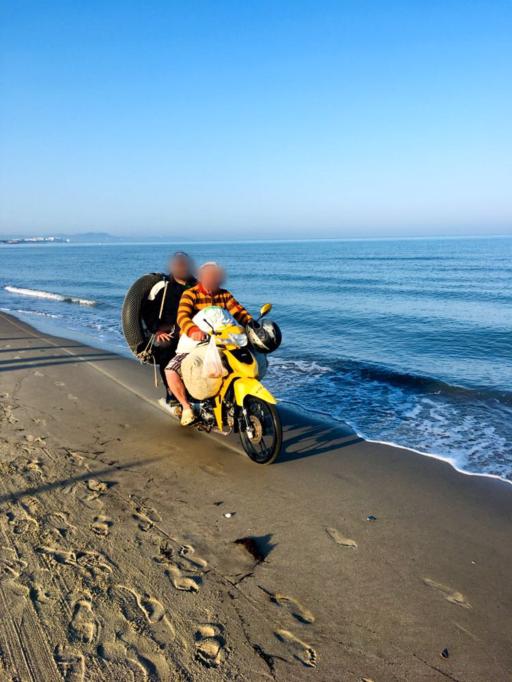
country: AL
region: Tirane
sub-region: Rrethi i Kavajes
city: Golem
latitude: 41.2421
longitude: 19.5172
